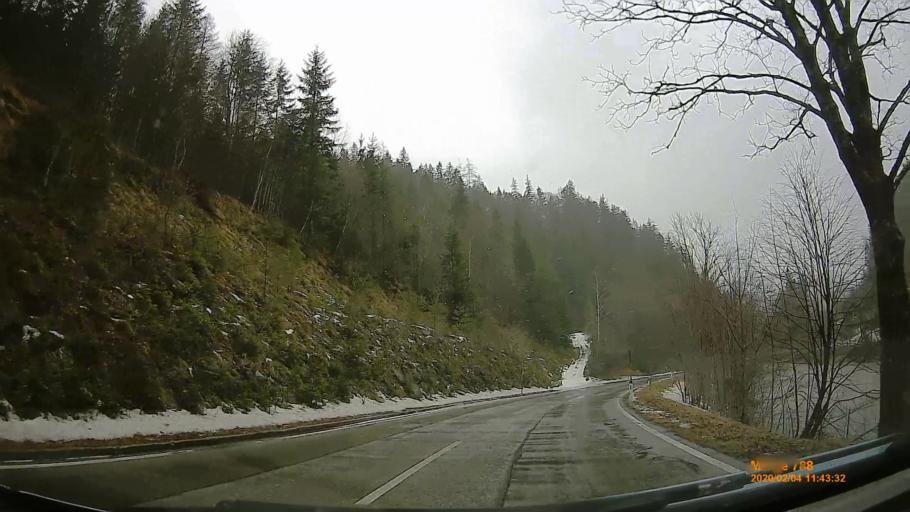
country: AT
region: Styria
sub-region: Politischer Bezirk Bruck-Muerzzuschlag
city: Muerzsteg
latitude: 47.6807
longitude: 15.4846
